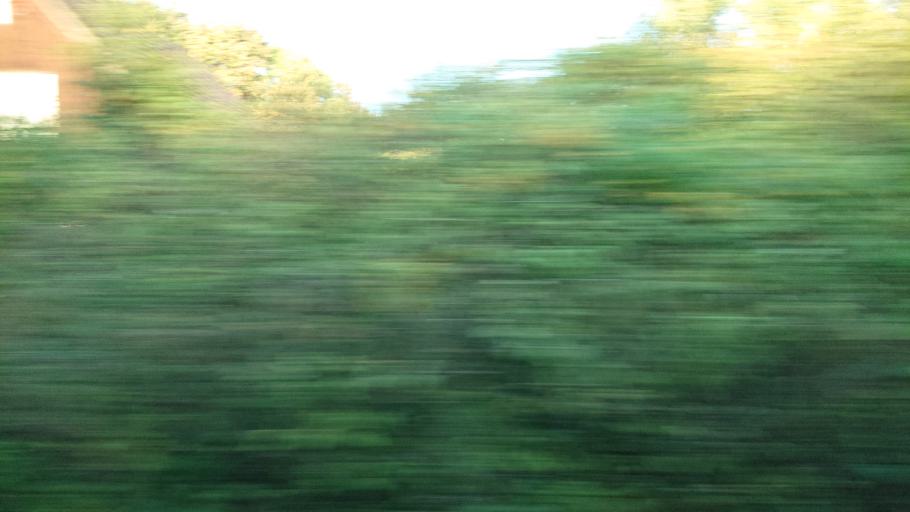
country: DE
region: Mecklenburg-Vorpommern
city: Trollenhagen
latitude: 53.6346
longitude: 13.2663
